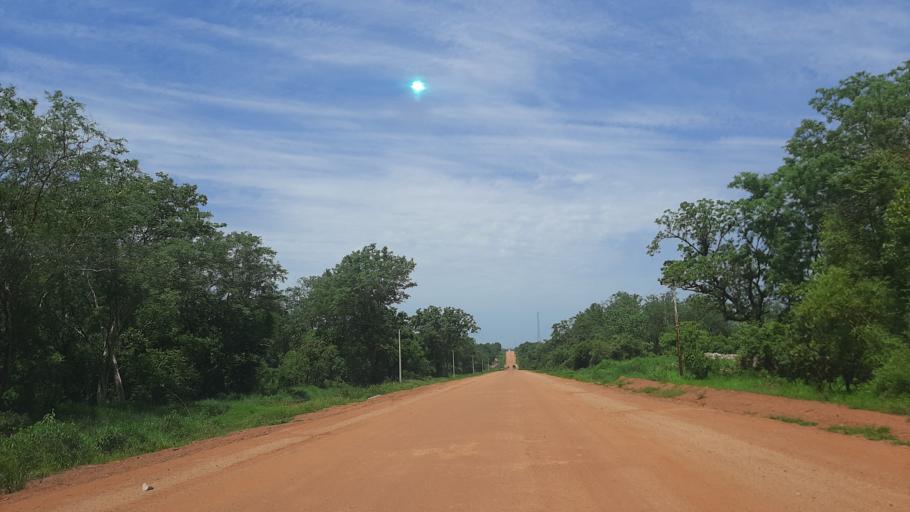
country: ET
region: Gambela
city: Gambela
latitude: 8.0733
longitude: 34.5890
